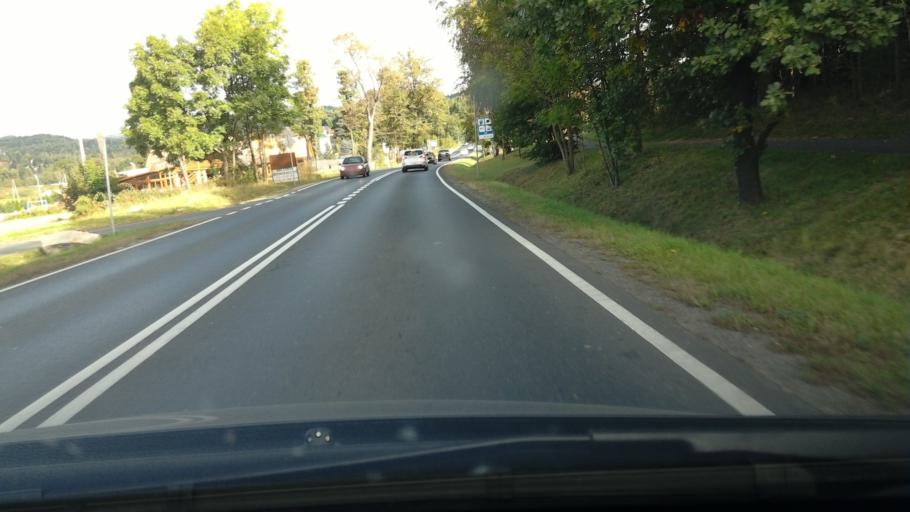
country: PL
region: Lower Silesian Voivodeship
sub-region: Jelenia Gora
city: Jelenia Gora
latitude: 50.8765
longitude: 15.7590
